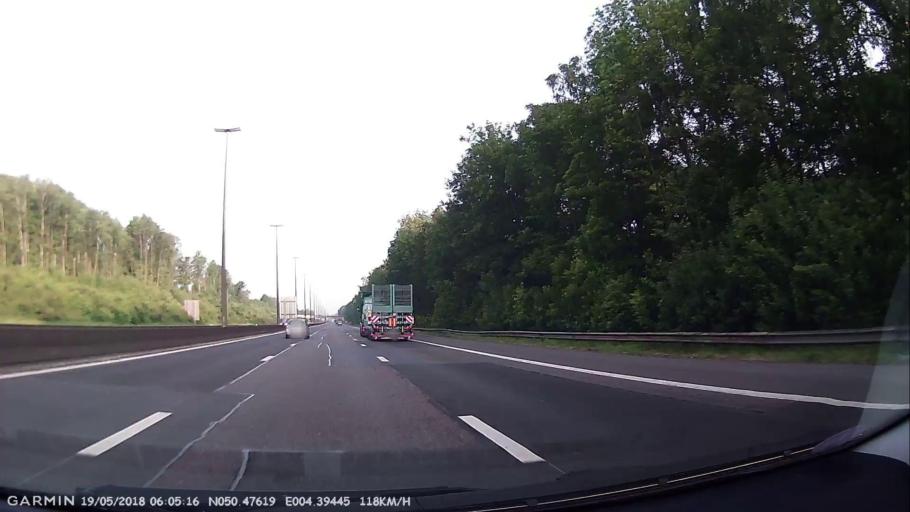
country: BE
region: Wallonia
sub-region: Province du Hainaut
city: Courcelles
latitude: 50.4762
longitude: 4.3943
